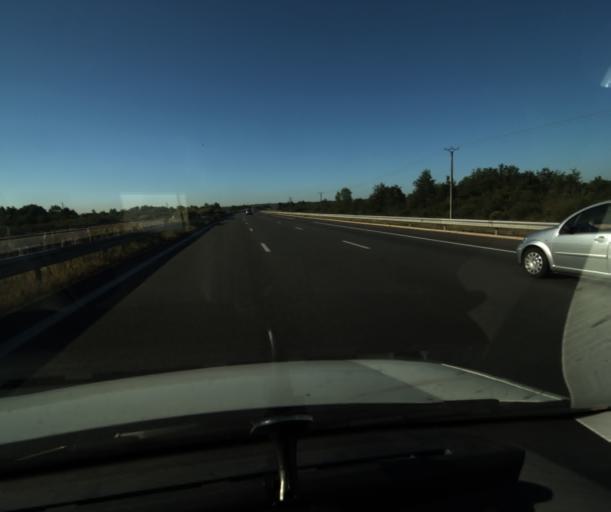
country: FR
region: Midi-Pyrenees
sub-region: Departement du Tarn-et-Garonne
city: Campsas
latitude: 43.8701
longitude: 1.3182
